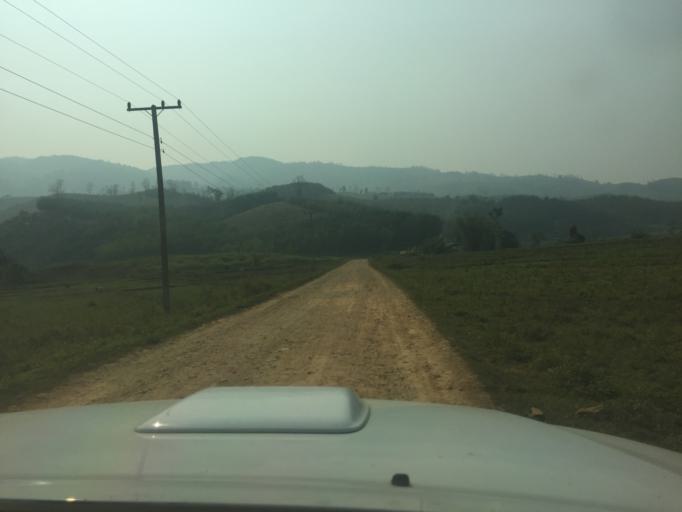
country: TH
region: Phayao
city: Phu Sang
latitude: 19.6699
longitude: 100.5269
